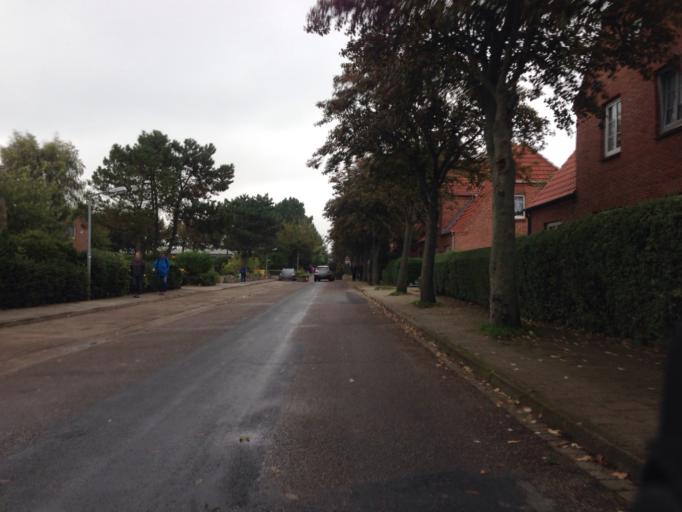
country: DE
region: Schleswig-Holstein
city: Wyk auf Fohr
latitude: 54.6876
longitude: 8.5623
